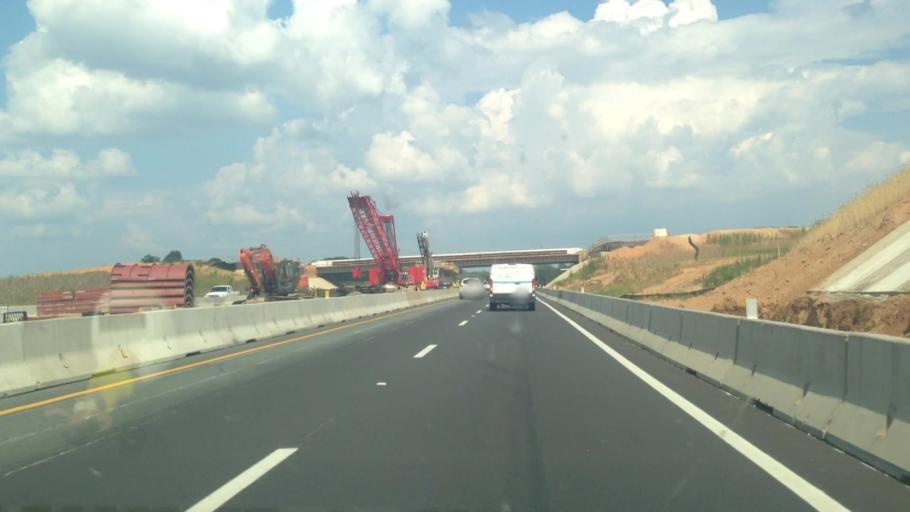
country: US
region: North Carolina
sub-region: Forsyth County
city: Kernersville
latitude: 36.1128
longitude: -80.1324
